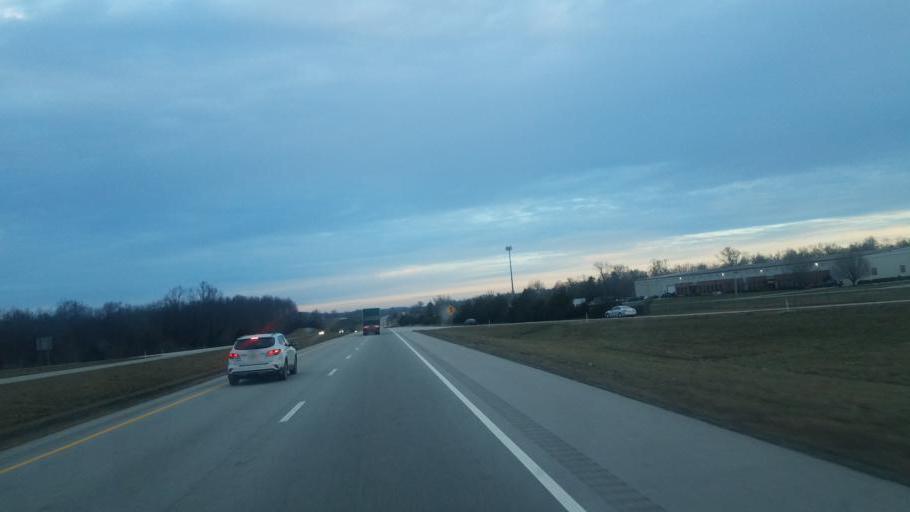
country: US
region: Tennessee
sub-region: Putnam County
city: Cookeville
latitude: 36.0574
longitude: -85.5073
